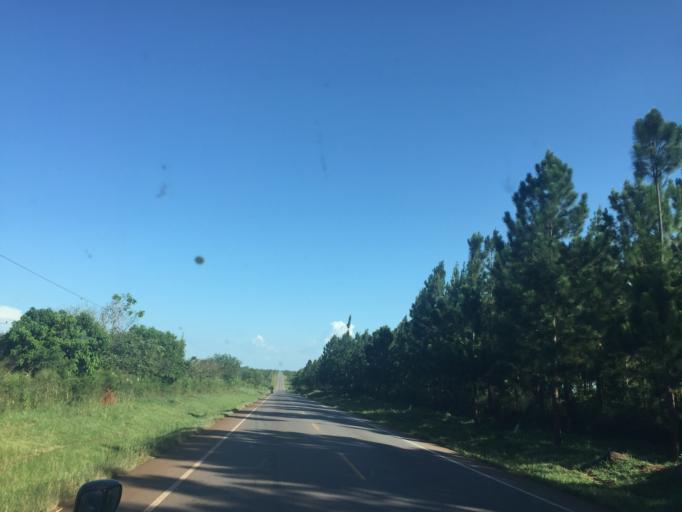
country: UG
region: Central Region
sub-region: Nakasongola District
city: Nakasongola
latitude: 1.3742
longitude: 32.3481
